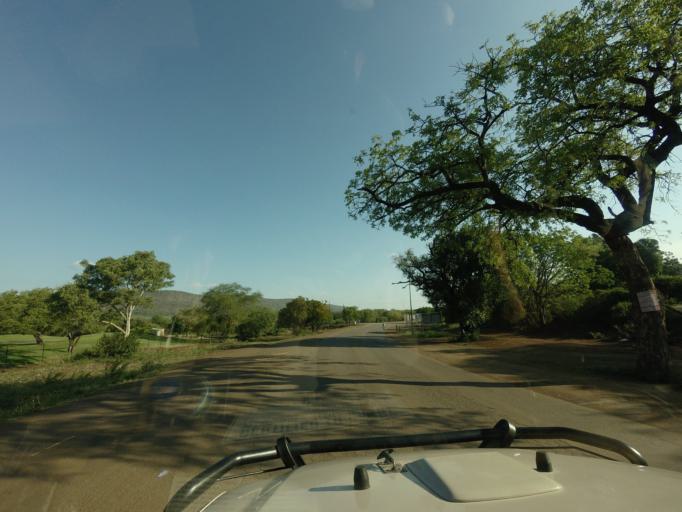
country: ZA
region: Mpumalanga
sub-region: Ehlanzeni District
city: Komatipoort
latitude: -25.4398
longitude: 31.9618
